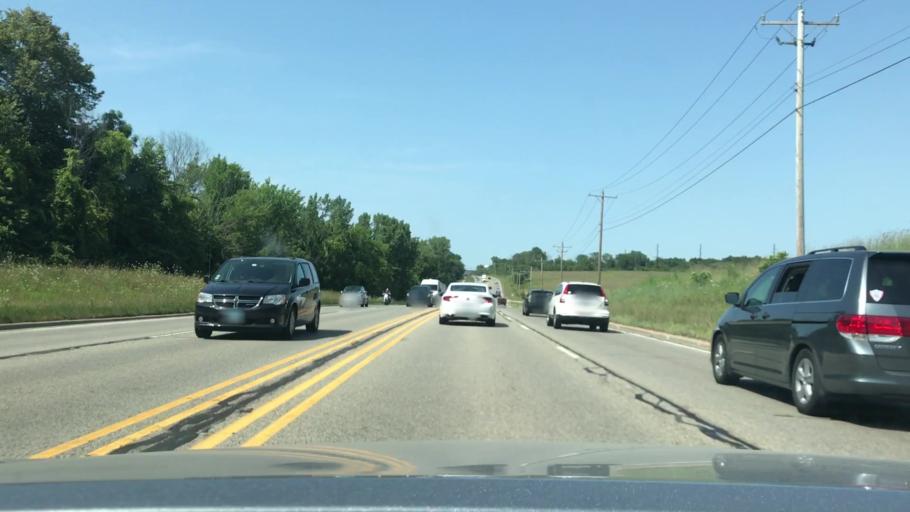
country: US
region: Illinois
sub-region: Kane County
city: Batavia
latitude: 41.8427
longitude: -88.2795
